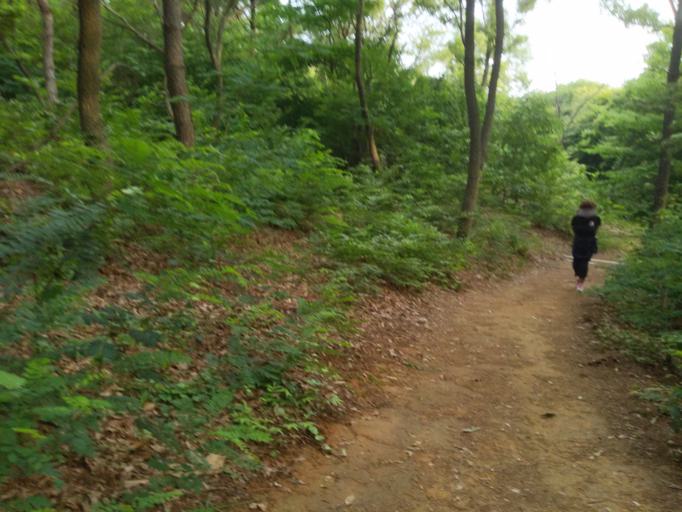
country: KR
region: Daegu
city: Hwawon
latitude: 35.8002
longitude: 128.5270
